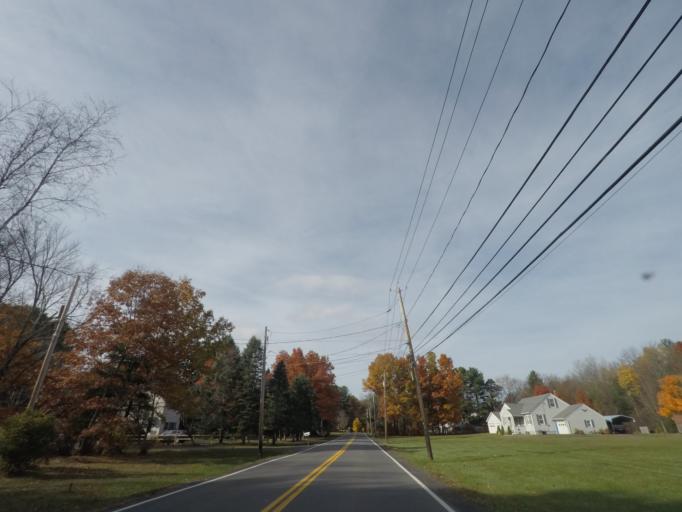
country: US
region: New York
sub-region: Schenectady County
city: Rotterdam
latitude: 42.7540
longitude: -73.9573
